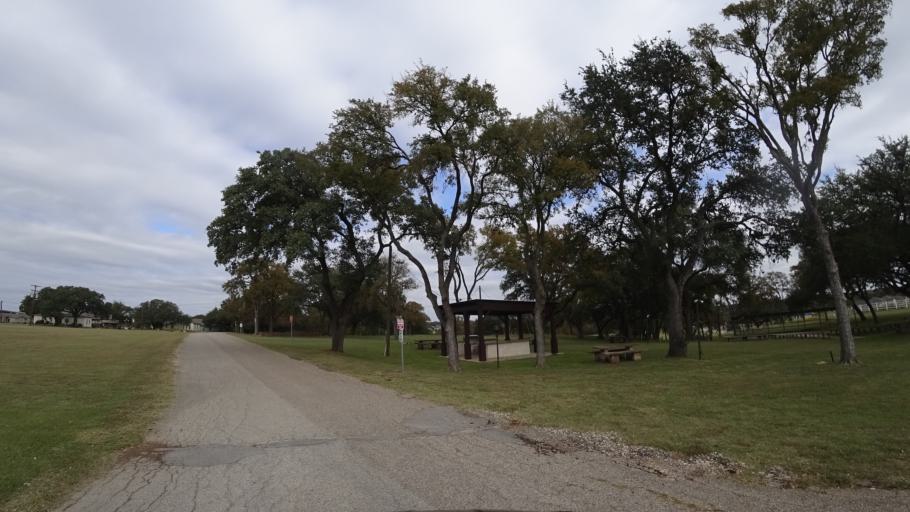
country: US
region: Texas
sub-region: Travis County
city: Manchaca
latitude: 30.1368
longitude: -97.8521
